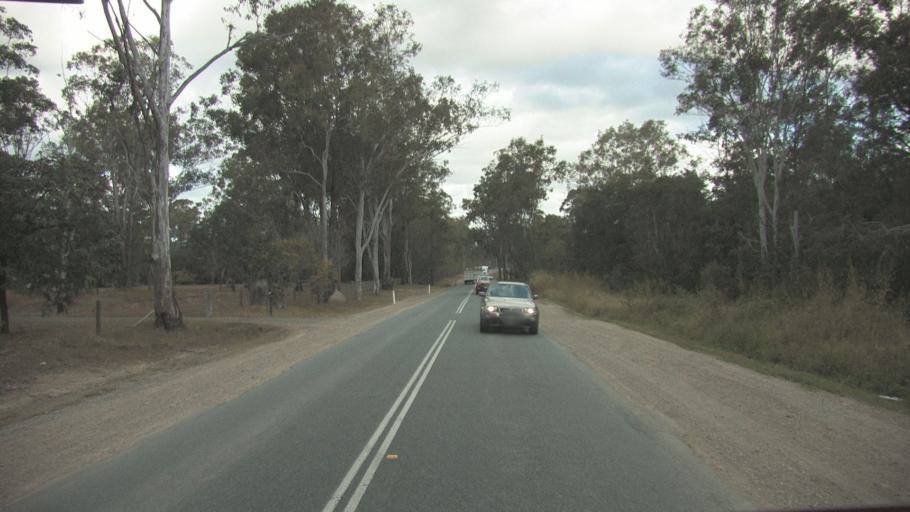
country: AU
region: Queensland
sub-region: Logan
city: Cedar Vale
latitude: -27.8486
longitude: 153.0509
